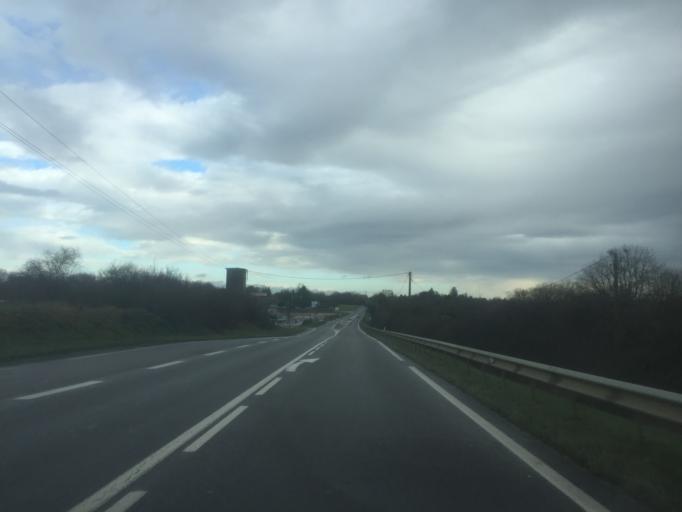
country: FR
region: Franche-Comte
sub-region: Departement du Jura
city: Fraisans
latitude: 47.1712
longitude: 5.7788
